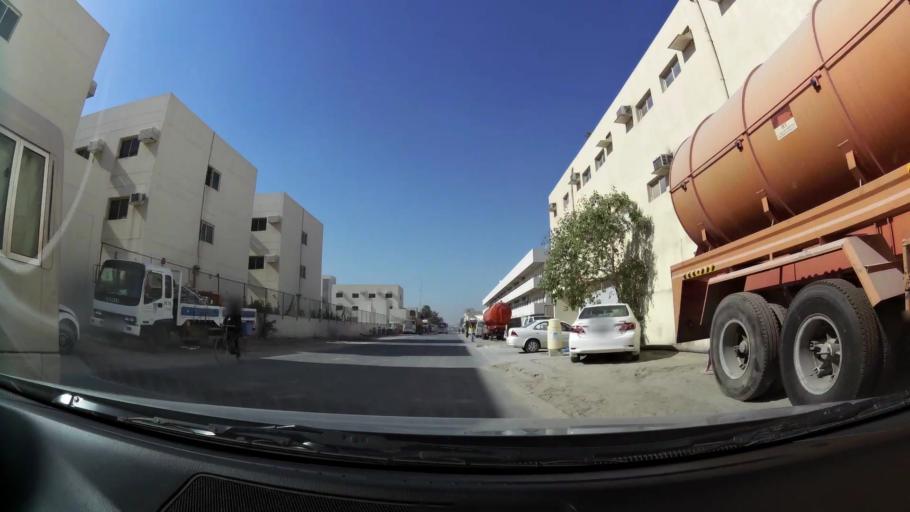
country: AE
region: Dubai
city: Dubai
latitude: 25.0080
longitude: 55.1028
